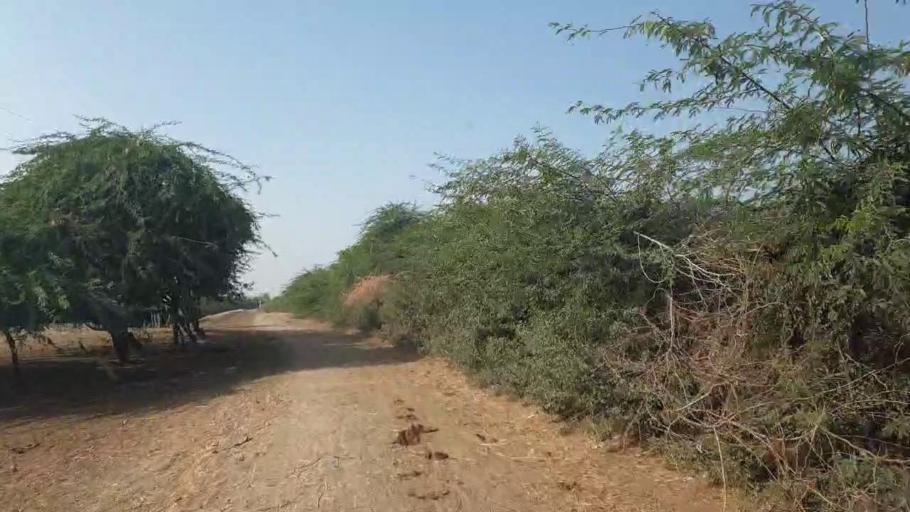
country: PK
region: Sindh
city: Badin
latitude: 24.5194
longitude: 68.7847
